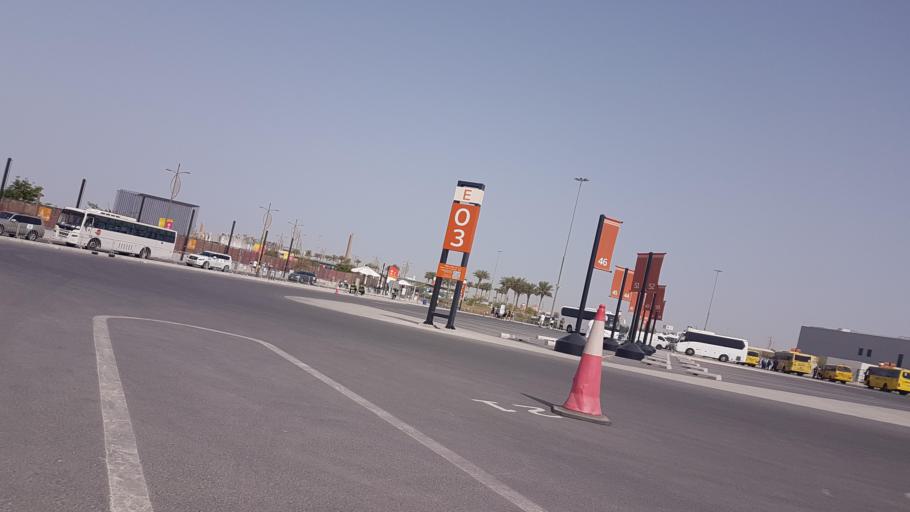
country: AE
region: Dubai
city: Dubai
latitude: 24.9659
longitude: 55.1571
